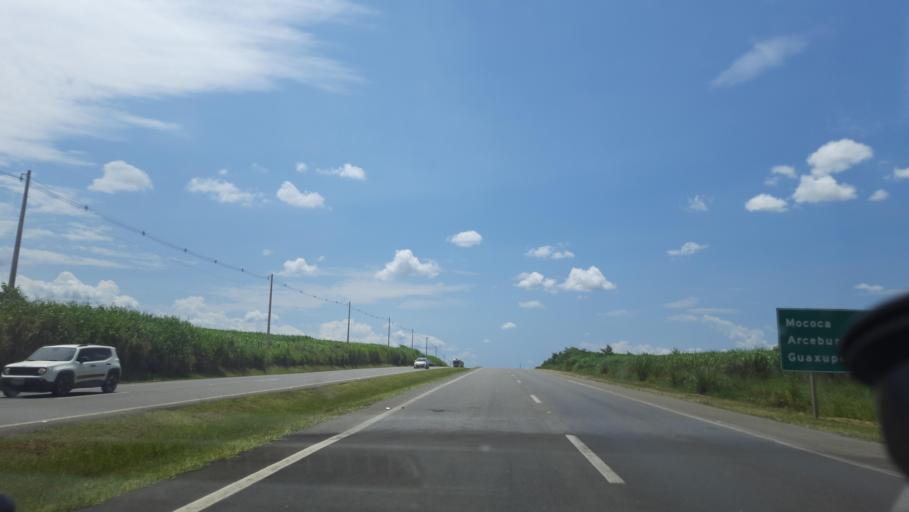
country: BR
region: Sao Paulo
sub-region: Mococa
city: Mococa
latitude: -21.6012
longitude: -47.0411
